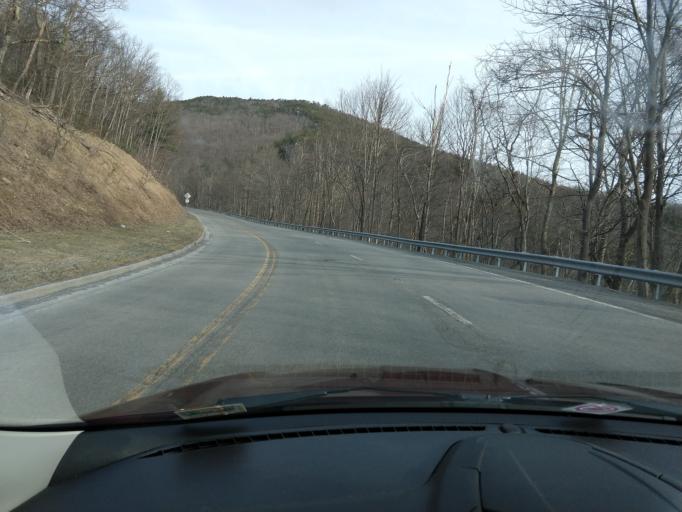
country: US
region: West Virginia
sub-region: Pendleton County
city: Franklin
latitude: 38.6981
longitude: -79.4050
